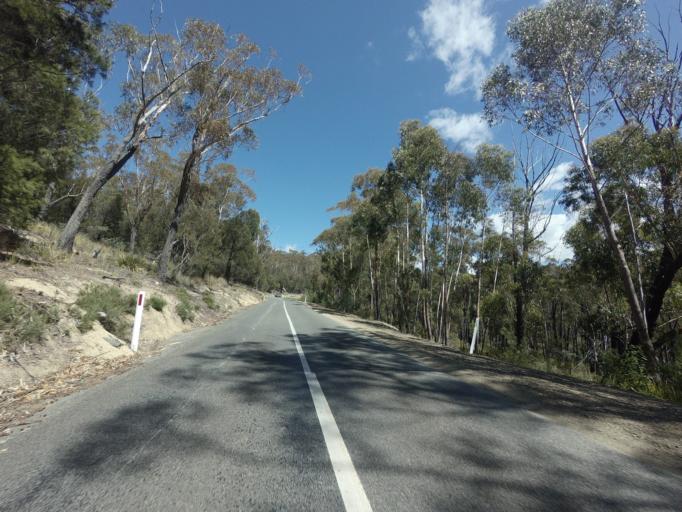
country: AU
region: Tasmania
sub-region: Break O'Day
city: St Helens
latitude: -41.6630
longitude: 148.2692
